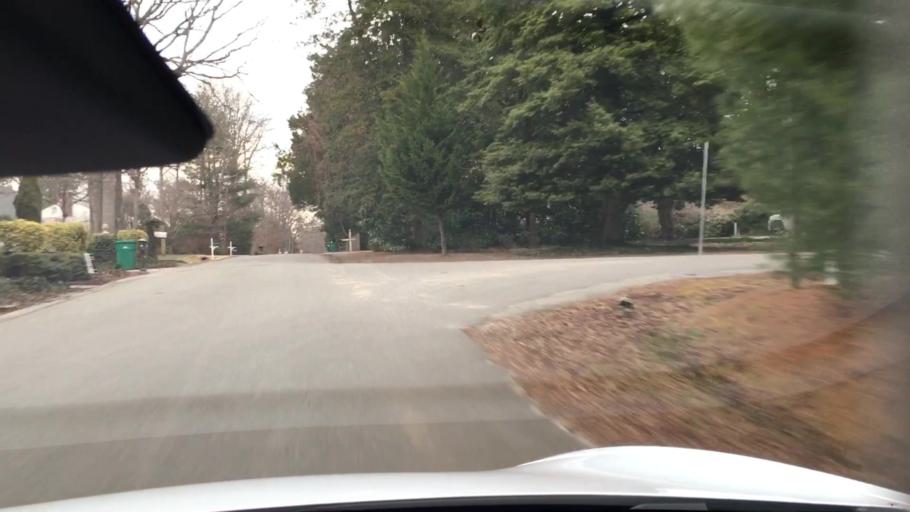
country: US
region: Virginia
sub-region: Chesterfield County
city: Bon Air
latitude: 37.5307
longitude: -77.5708
